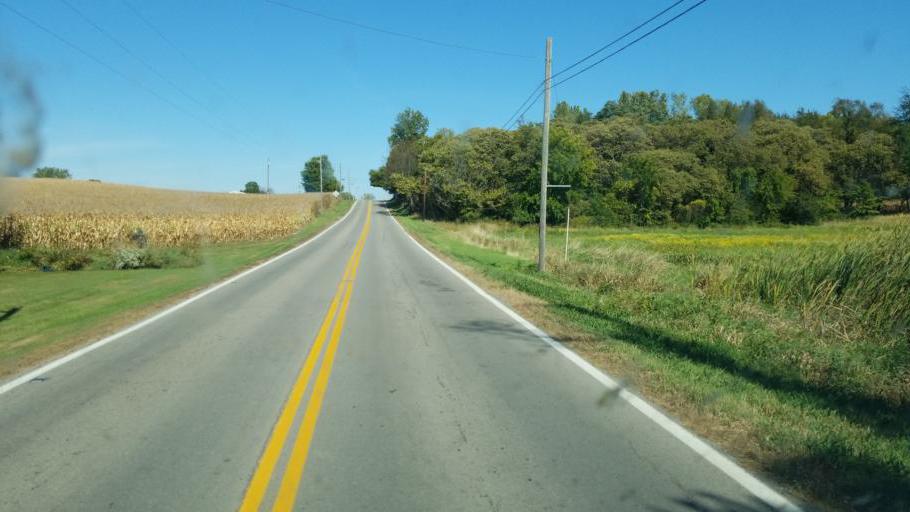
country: US
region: Ohio
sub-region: Huron County
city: Plymouth
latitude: 40.9962
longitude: -82.7012
